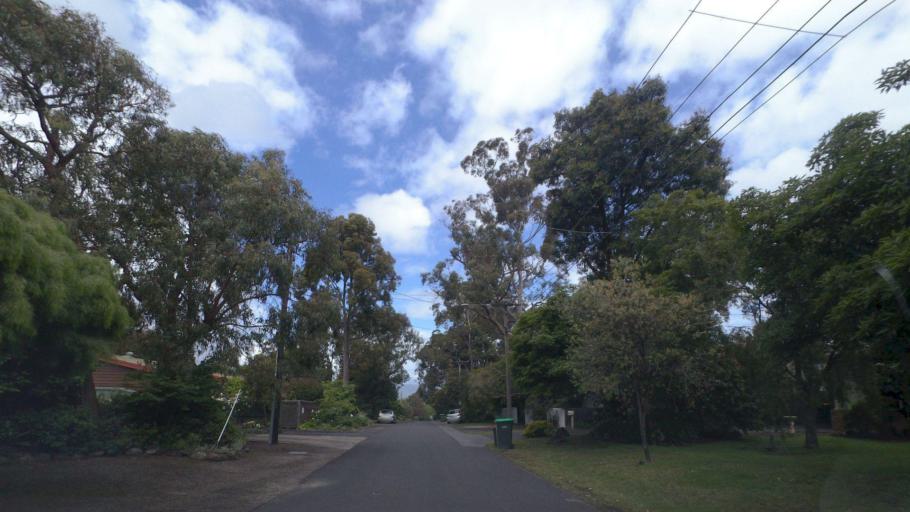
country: AU
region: Victoria
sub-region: Whitehorse
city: Vermont
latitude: -37.8335
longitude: 145.1970
